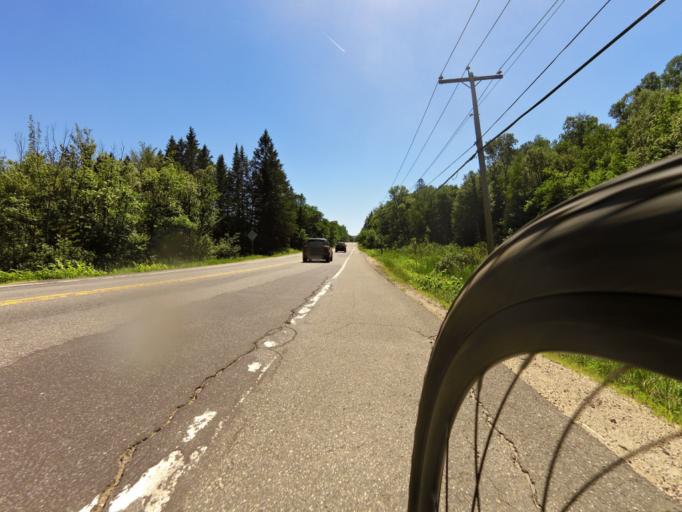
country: CA
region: Quebec
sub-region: Laurentides
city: Mont-Tremblant
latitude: 46.0999
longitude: -74.6178
